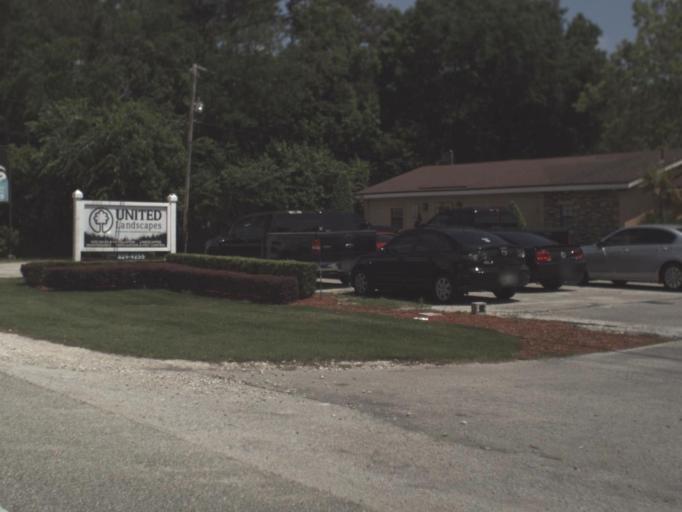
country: US
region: Florida
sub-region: Saint Johns County
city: Villano Beach
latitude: 29.9826
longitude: -81.3650
